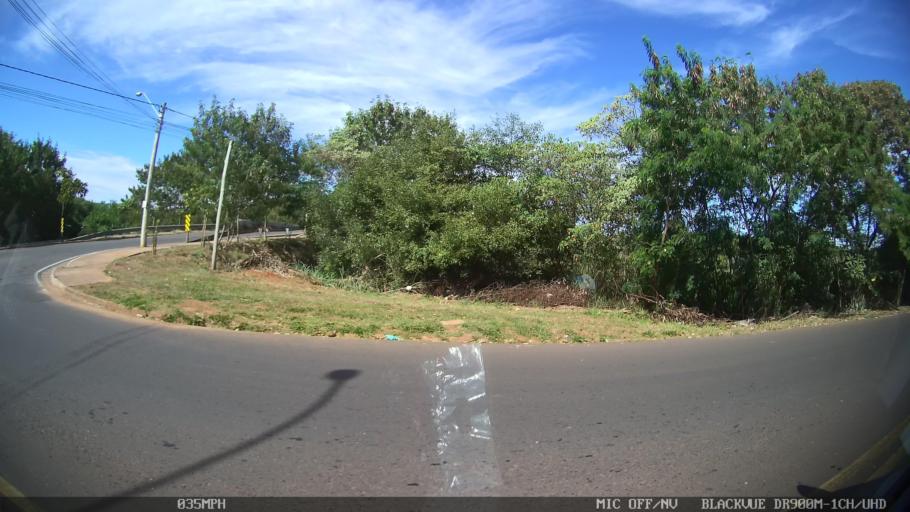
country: BR
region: Sao Paulo
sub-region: Sao Jose Do Rio Preto
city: Sao Jose do Rio Preto
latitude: -20.8454
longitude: -49.3595
